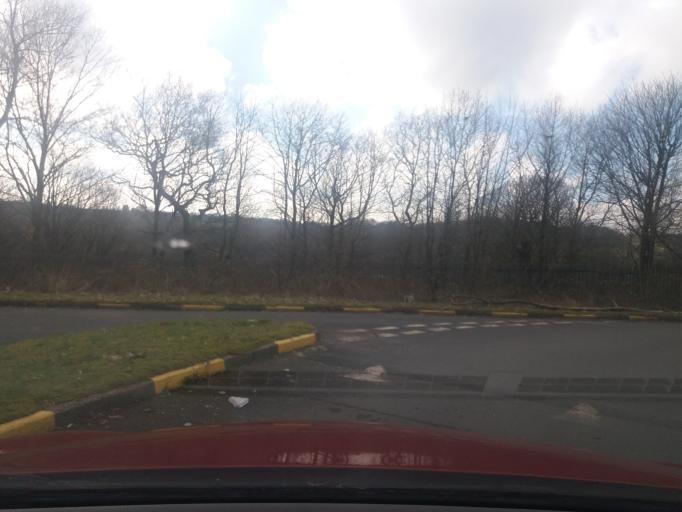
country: GB
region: England
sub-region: Lancashire
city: Coppull
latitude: 53.6346
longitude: -2.6488
